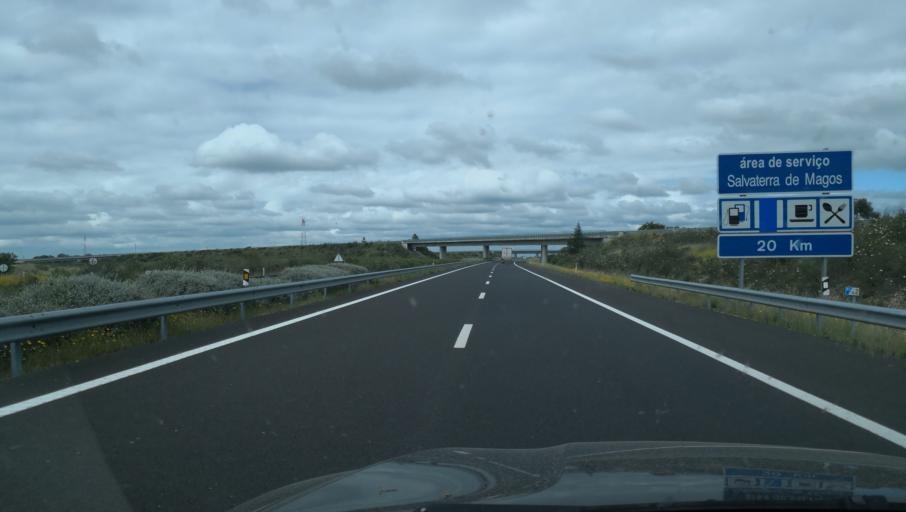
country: PT
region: Santarem
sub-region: Benavente
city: Poceirao
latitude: 38.9007
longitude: -8.7840
